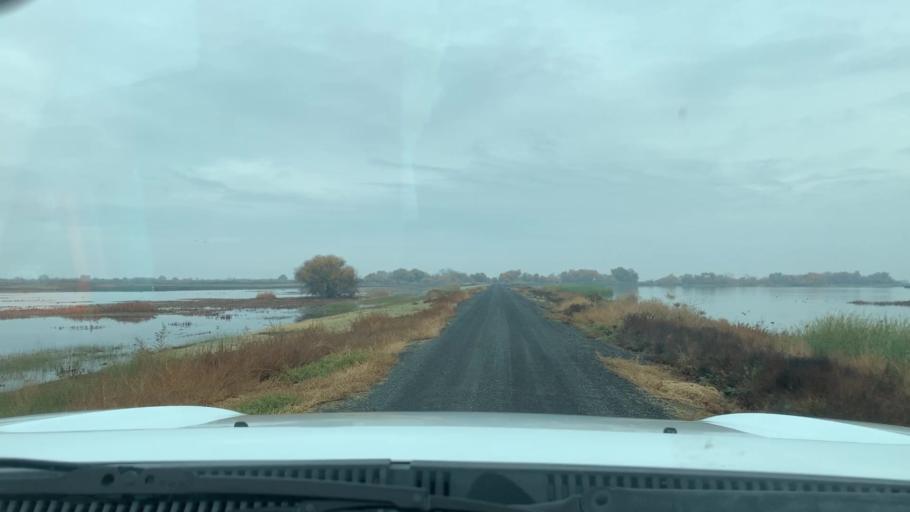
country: US
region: California
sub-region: Kern County
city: Lost Hills
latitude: 35.7475
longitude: -119.6034
